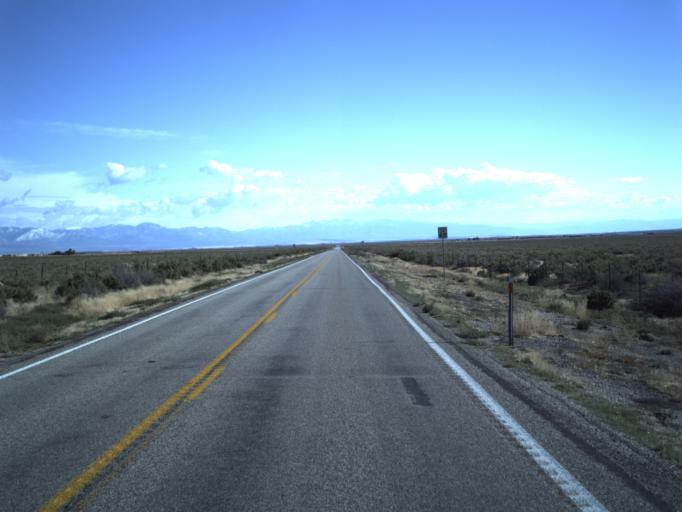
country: US
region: Utah
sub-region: Millard County
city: Delta
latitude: 39.3470
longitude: -112.4954
